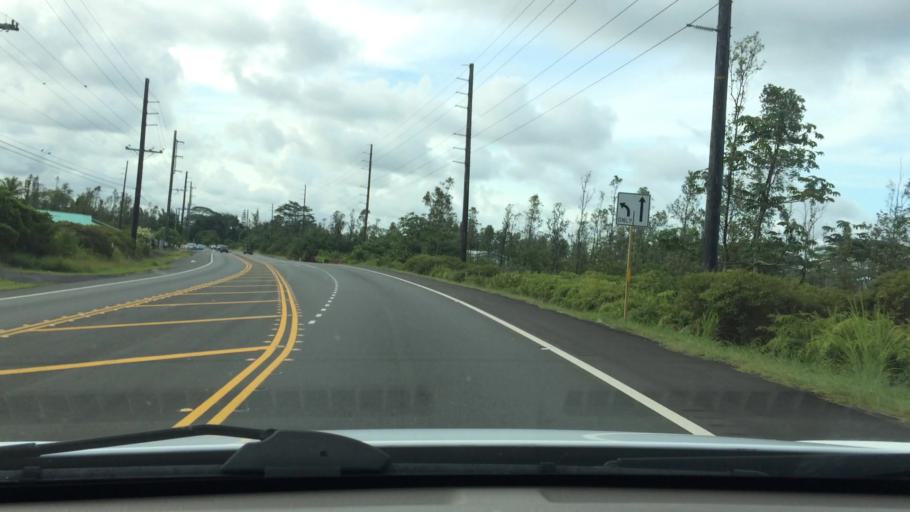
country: US
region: Hawaii
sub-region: Hawaii County
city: Ainaloa
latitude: 19.5418
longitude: -154.9738
